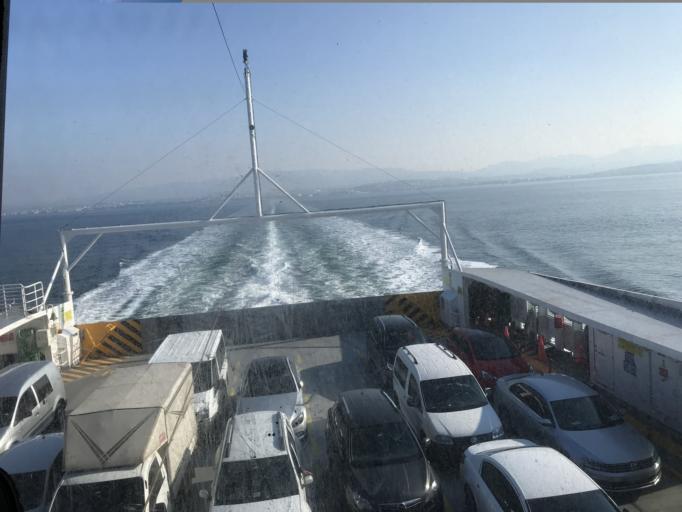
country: TR
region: Yalova
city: Yalova
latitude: 40.6947
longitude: 29.2519
